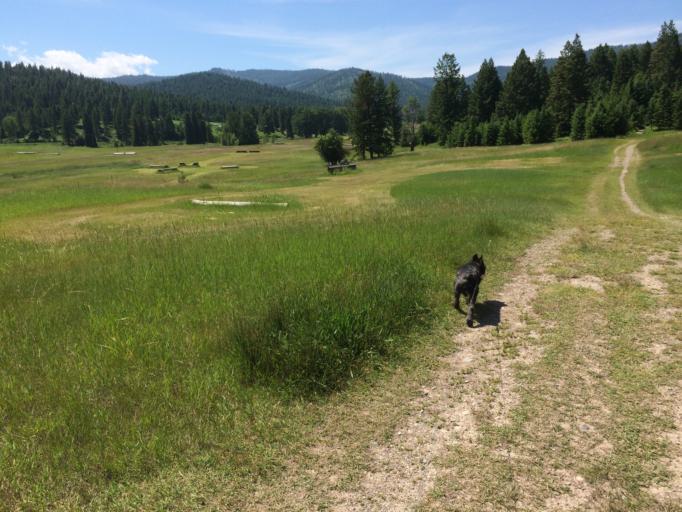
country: US
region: Montana
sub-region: Flathead County
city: Kalispell
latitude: 48.1504
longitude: -114.3556
